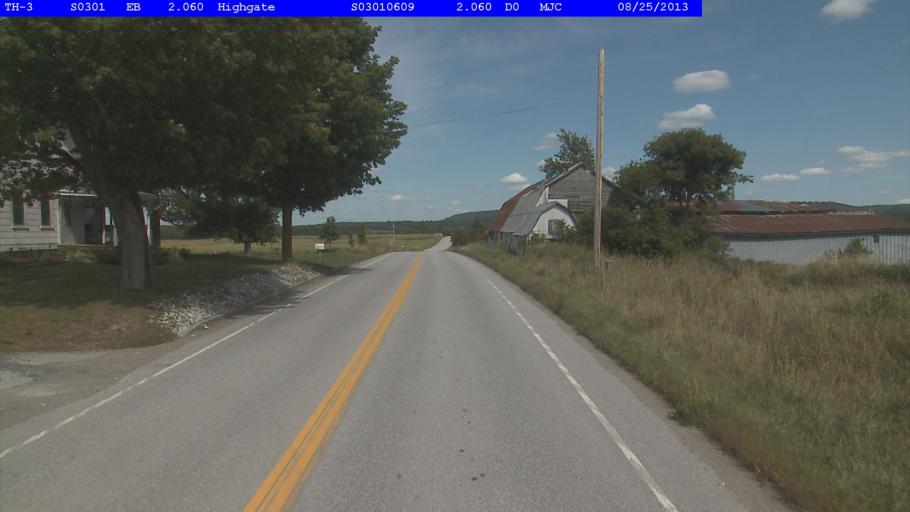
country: US
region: Vermont
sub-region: Franklin County
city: Swanton
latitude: 44.9642
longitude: -72.9823
